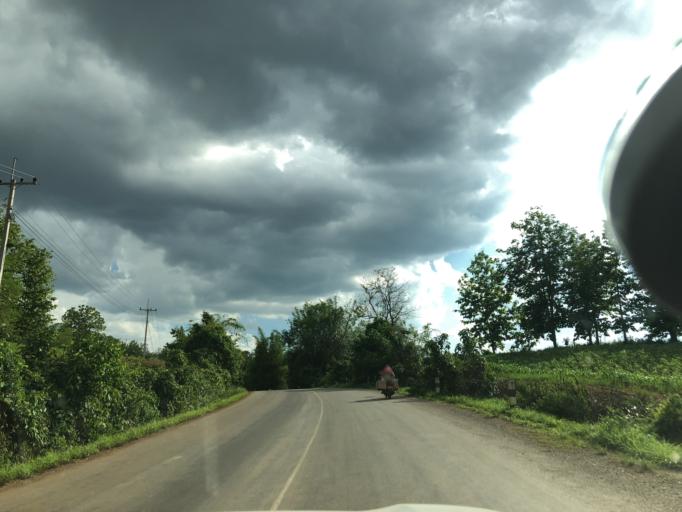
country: TH
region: Uttaradit
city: Ban Khok
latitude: 18.1274
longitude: 101.3748
